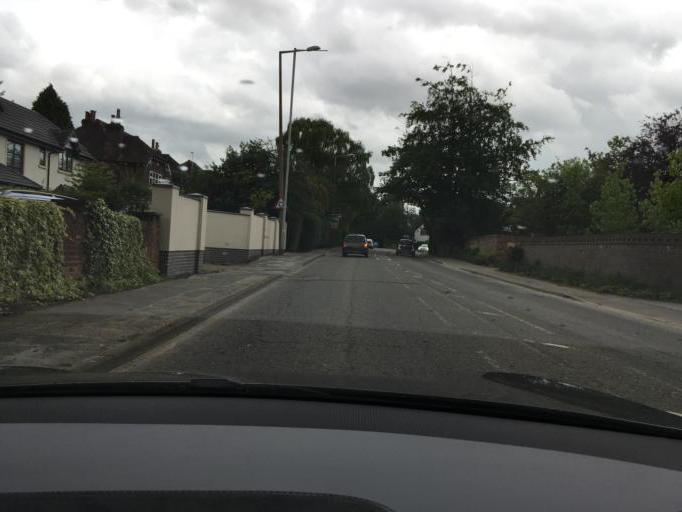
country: GB
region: England
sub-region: Borough of Stockport
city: Bramhall
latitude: 53.3456
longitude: -2.1587
